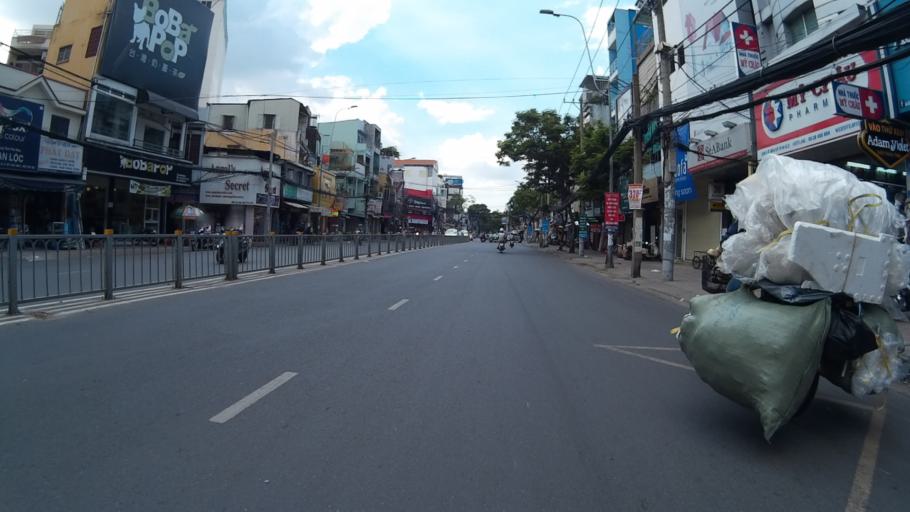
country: VN
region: Ho Chi Minh City
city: Quan Phu Nhuan
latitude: 10.7873
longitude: 106.6790
